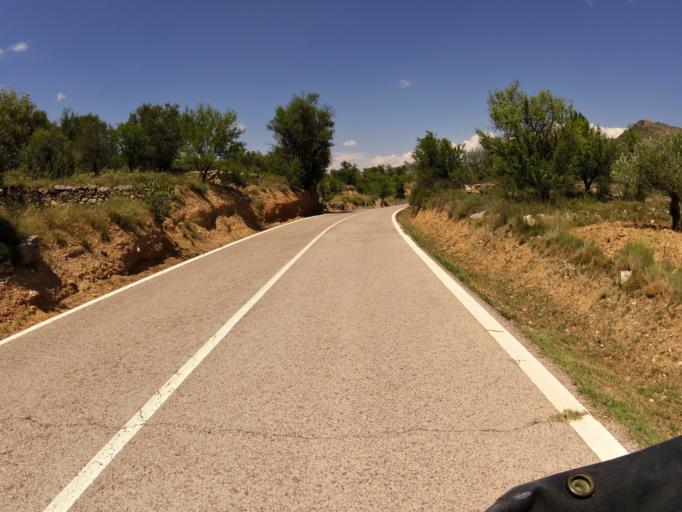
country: ES
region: Valencia
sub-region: Provincia de Valencia
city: Casas Bajas
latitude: 40.0154
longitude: -1.2667
